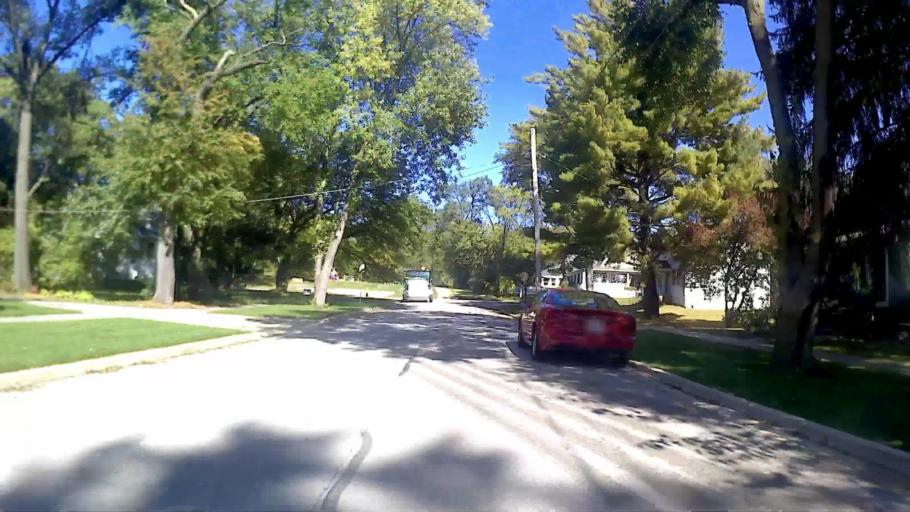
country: US
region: Illinois
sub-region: DuPage County
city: Glen Ellyn
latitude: 41.8787
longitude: -88.0499
